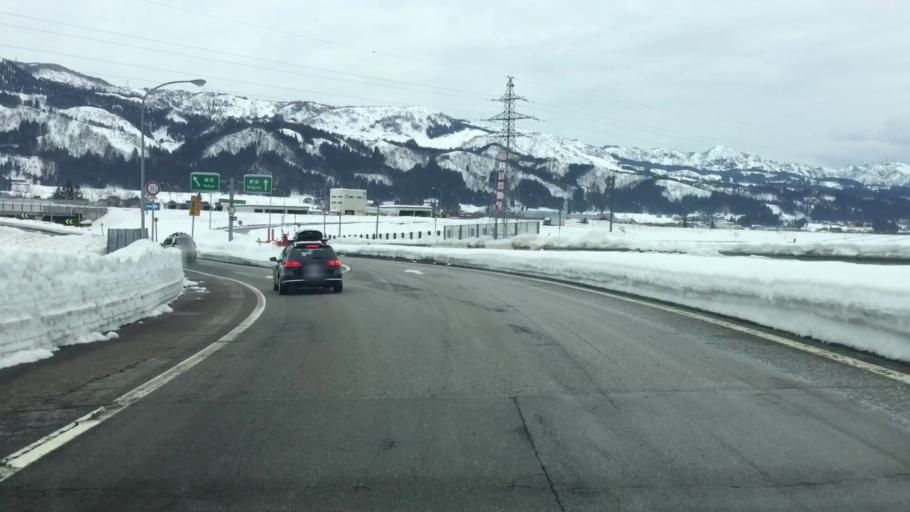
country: JP
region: Niigata
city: Shiozawa
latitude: 36.9954
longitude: 138.8215
